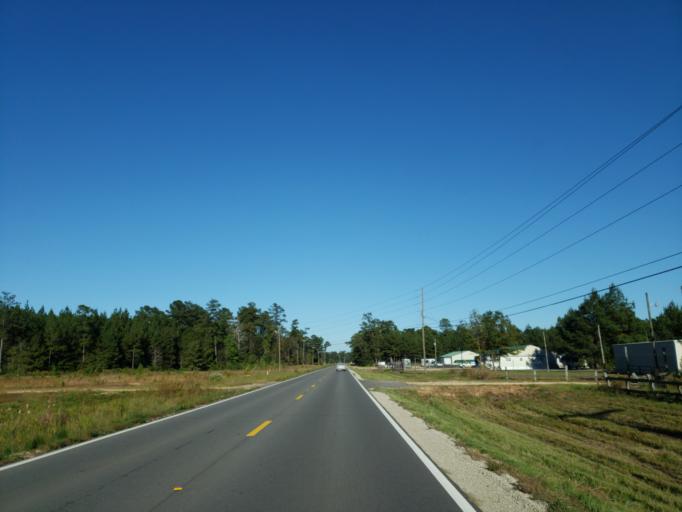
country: US
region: Mississippi
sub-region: Forrest County
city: Petal
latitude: 31.3673
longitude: -89.1364
